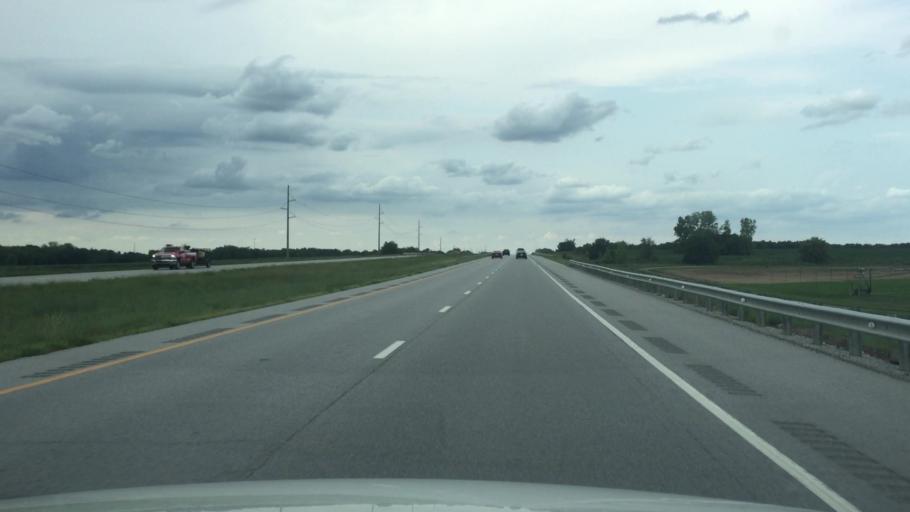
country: US
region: Kansas
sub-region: Miami County
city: Louisburg
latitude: 38.7053
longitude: -94.6763
